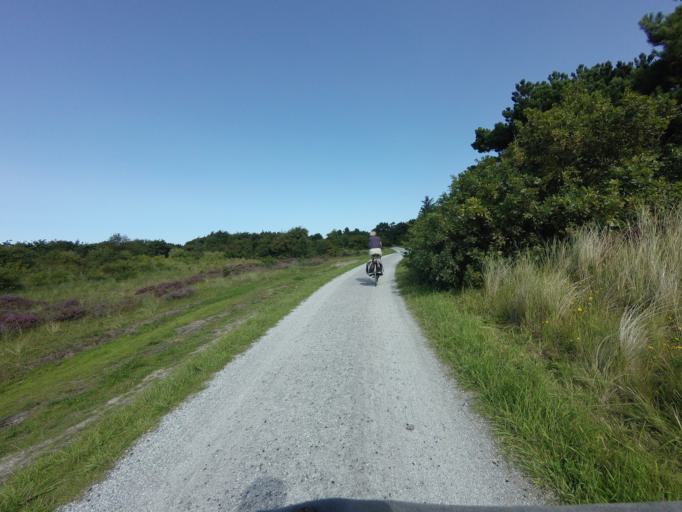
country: NL
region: Friesland
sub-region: Gemeente Terschelling
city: West-Terschelling
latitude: 53.3706
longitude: 5.2025
